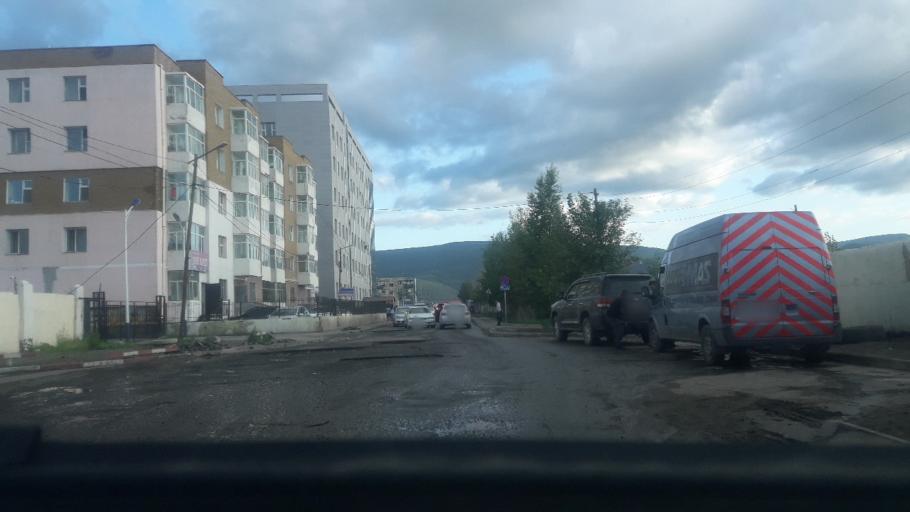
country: MN
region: Ulaanbaatar
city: Ulaanbaatar
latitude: 47.9160
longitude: 106.9945
